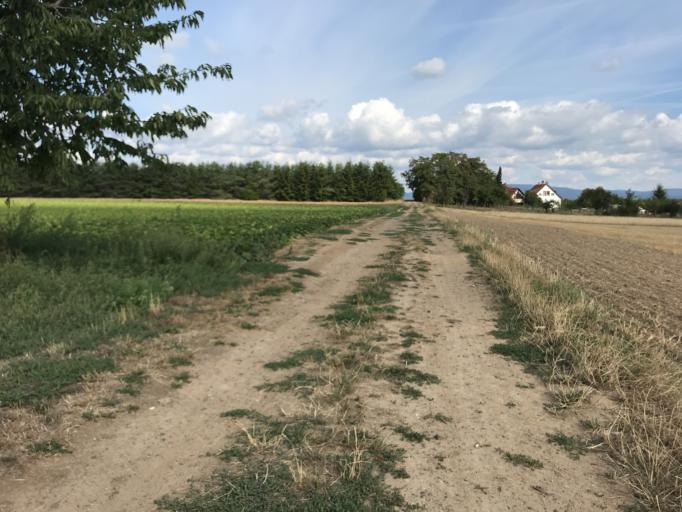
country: DE
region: Rheinland-Pfalz
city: Wackernheim
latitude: 49.9745
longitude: 8.1311
